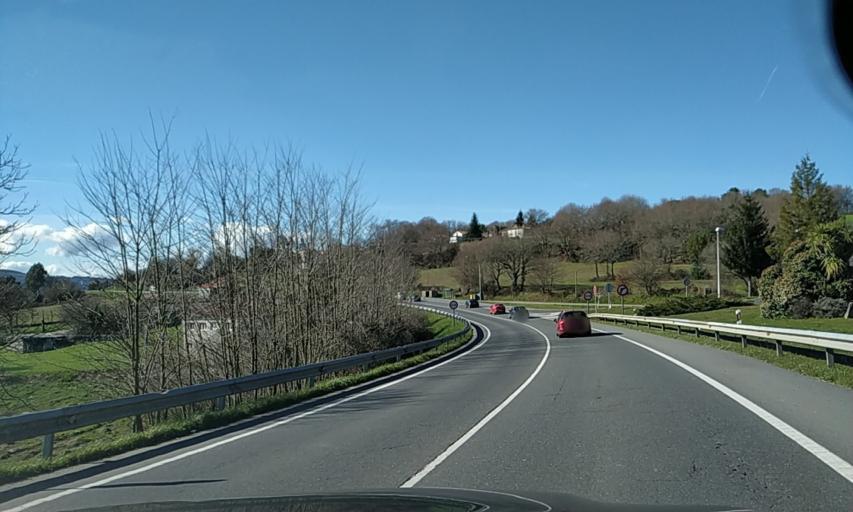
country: ES
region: Galicia
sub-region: Provincia de Pontevedra
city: Lalin
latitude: 42.6823
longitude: -8.1680
